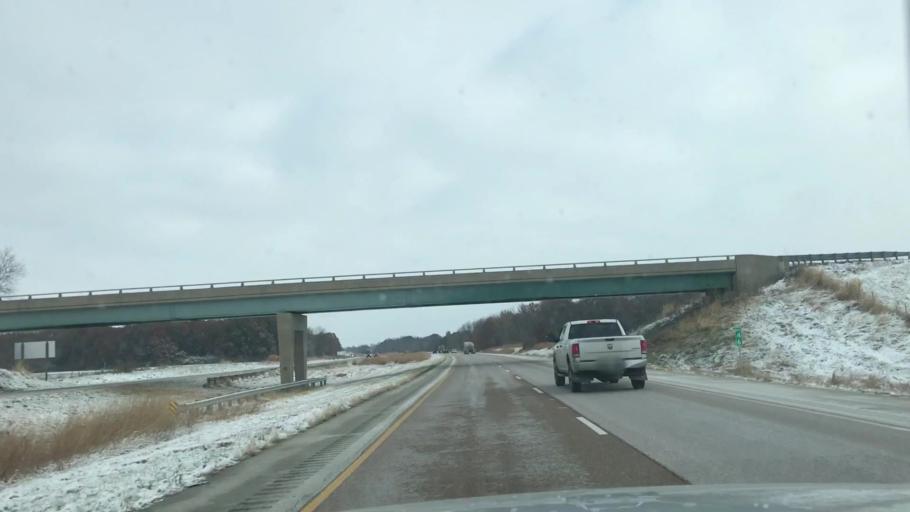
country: US
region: Illinois
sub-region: Macoupin County
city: Mount Olive
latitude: 39.0928
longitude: -89.7411
